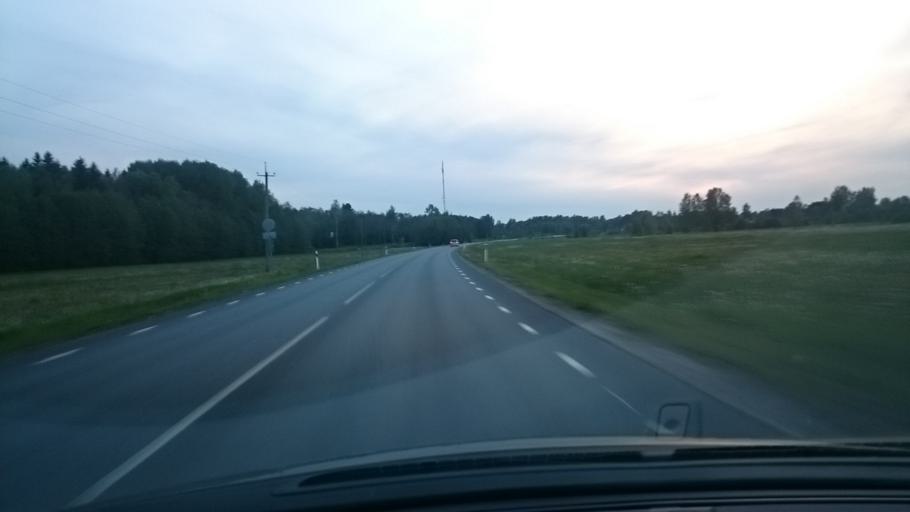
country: EE
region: Raplamaa
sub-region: Kehtna vald
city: Kehtna
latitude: 58.8546
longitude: 25.0091
